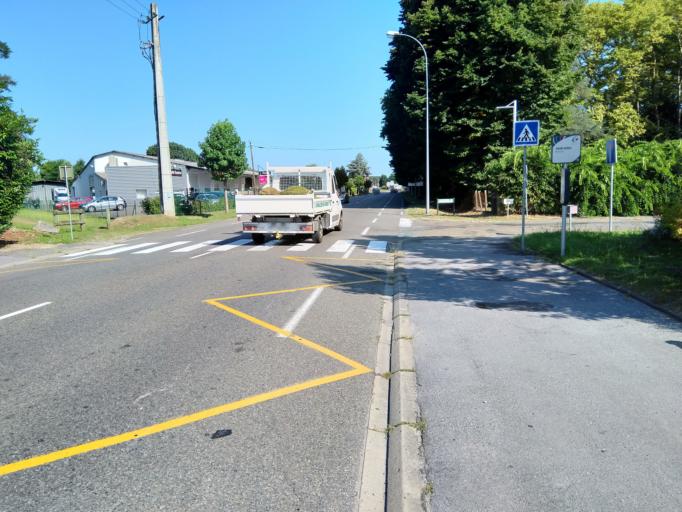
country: FR
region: Aquitaine
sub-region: Departement des Landes
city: Saint-Paul-les-Dax
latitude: 43.7416
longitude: -1.0539
